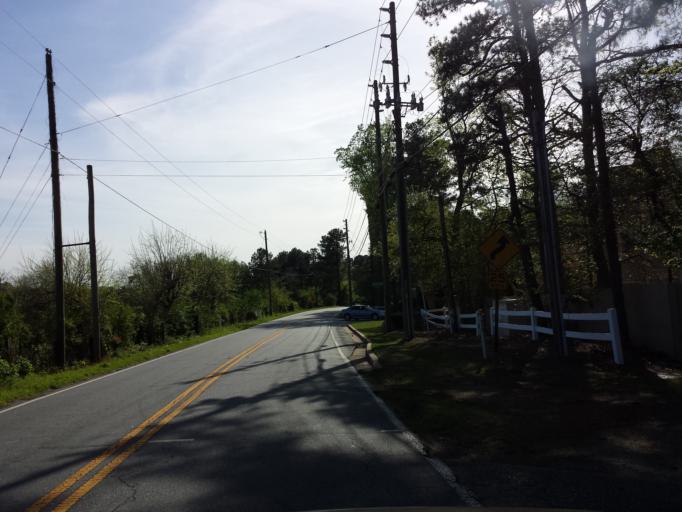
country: US
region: Georgia
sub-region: Cobb County
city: Marietta
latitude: 33.9677
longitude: -84.5094
